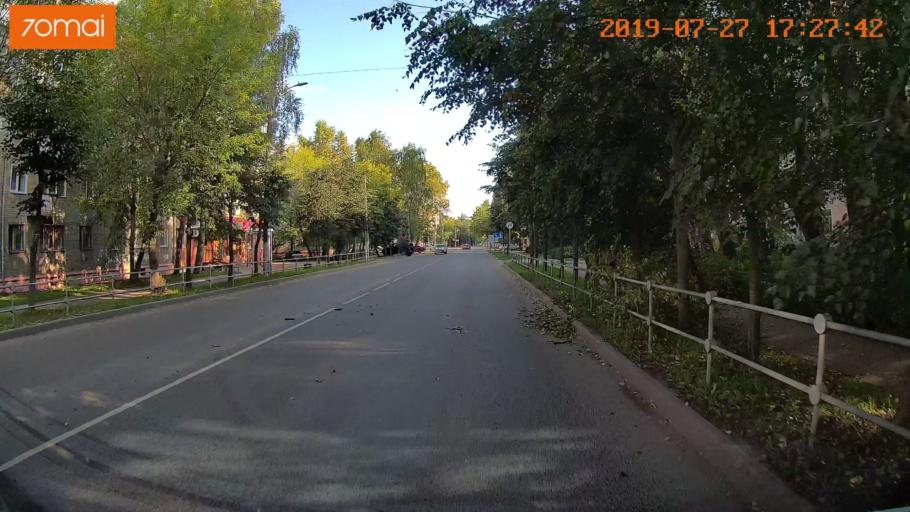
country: RU
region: Ivanovo
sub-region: Gorod Ivanovo
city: Ivanovo
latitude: 57.0127
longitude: 40.9788
